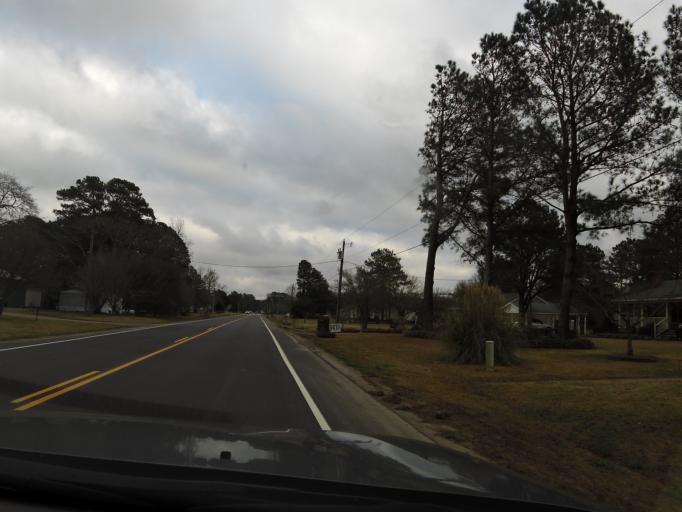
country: US
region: North Carolina
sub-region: Nash County
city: Rocky Mount
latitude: 35.8653
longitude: -77.7232
